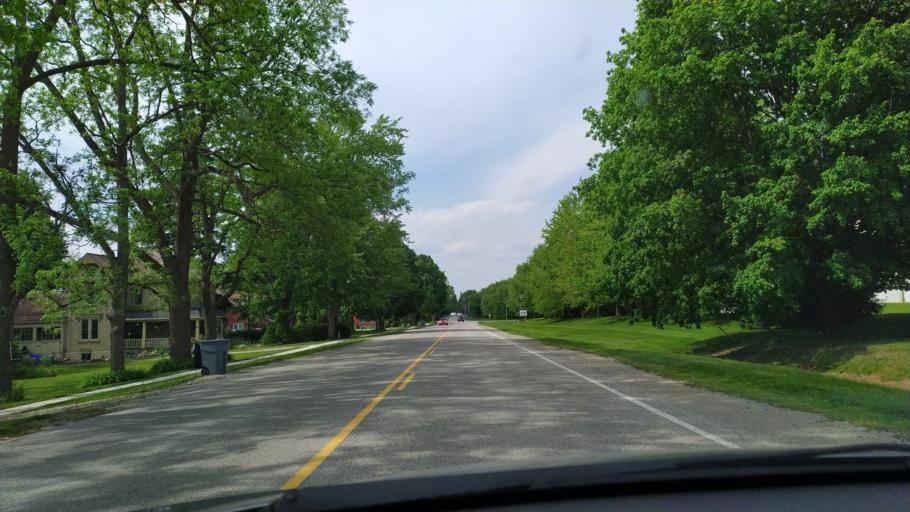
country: CA
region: Ontario
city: Ingersoll
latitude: 42.9848
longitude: -80.9524
